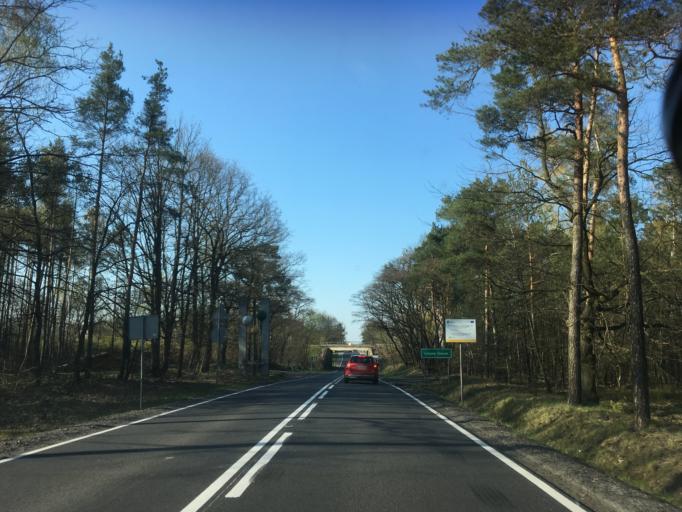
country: PL
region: Lubusz
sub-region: Powiat zaganski
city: Szprotawa
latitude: 51.4661
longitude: 15.6141
